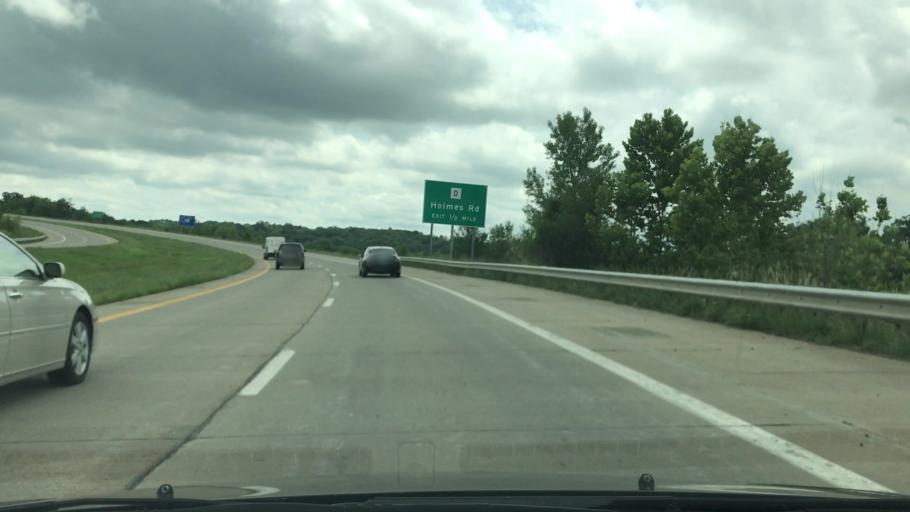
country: US
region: Missouri
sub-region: Jackson County
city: Grandview
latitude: 38.8664
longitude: -94.6007
